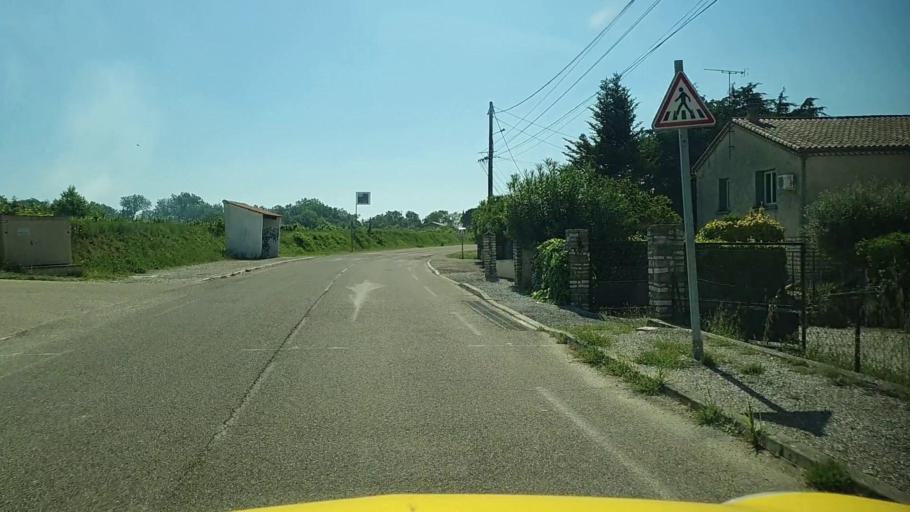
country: FR
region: Languedoc-Roussillon
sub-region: Departement du Gard
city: Moussac
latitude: 43.9856
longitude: 4.2283
